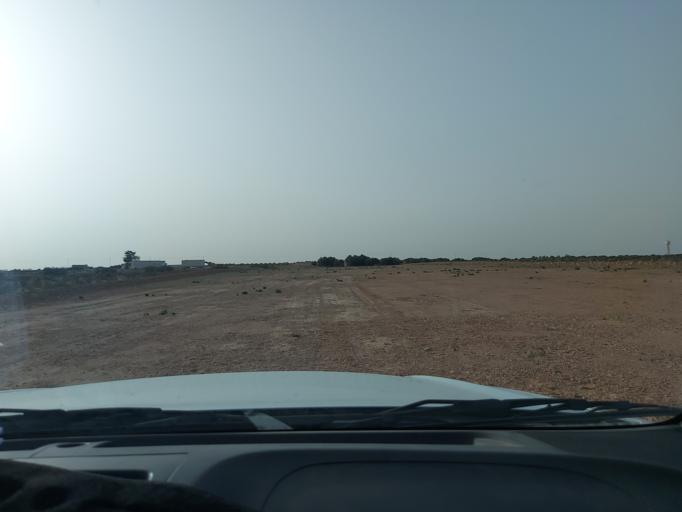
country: TN
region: Madanin
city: Medenine
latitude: 33.3376
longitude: 10.5946
